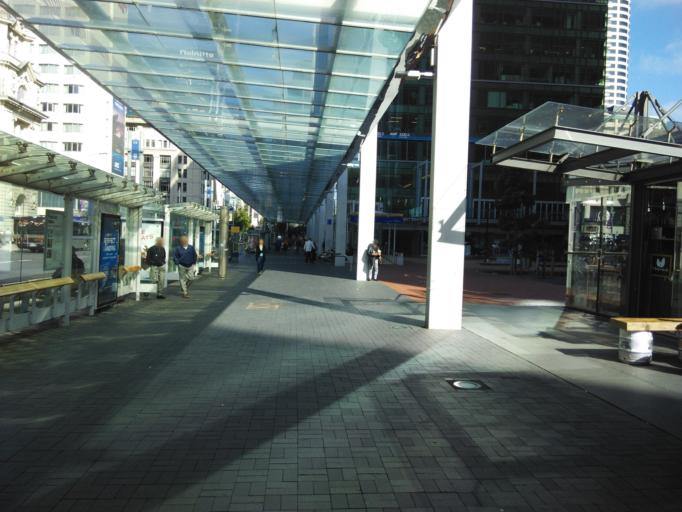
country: NZ
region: Auckland
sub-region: Auckland
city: Auckland
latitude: -36.8433
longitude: 174.7670
